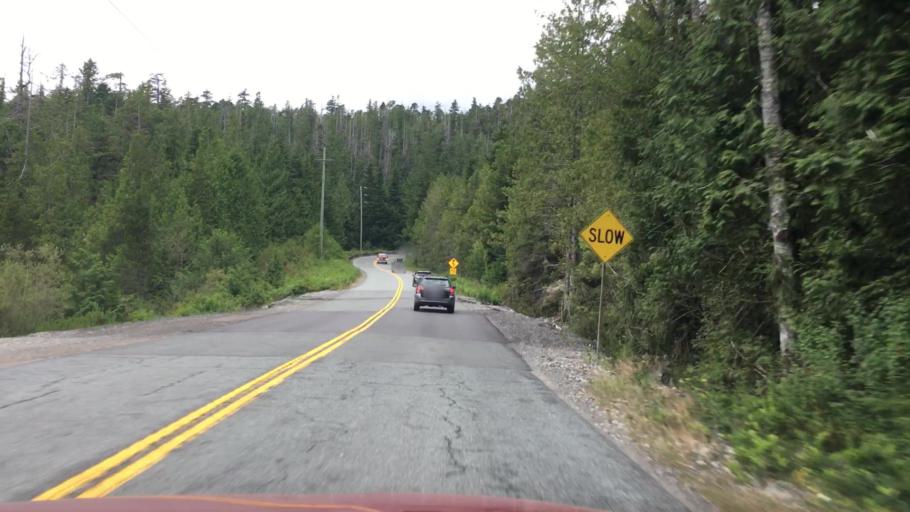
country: CA
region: British Columbia
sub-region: Regional District of Alberni-Clayoquot
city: Ucluelet
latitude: 49.1049
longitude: -125.4549
